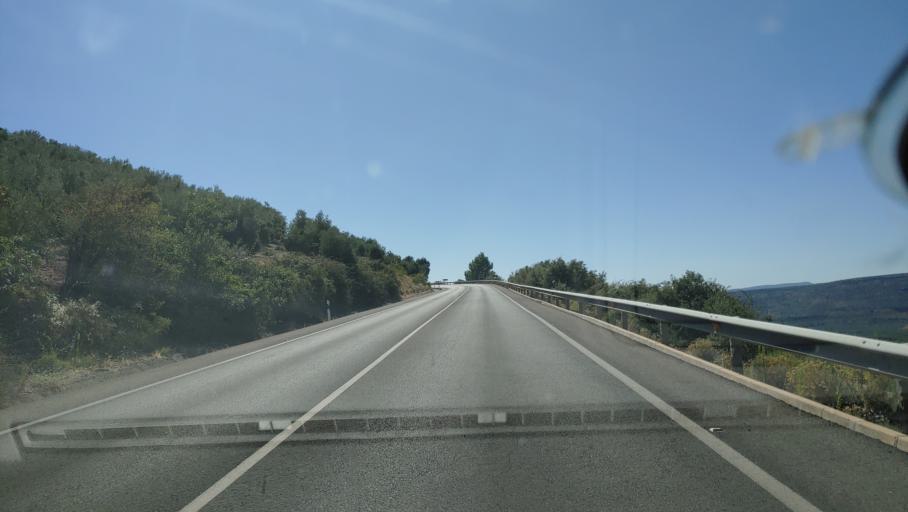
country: ES
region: Andalusia
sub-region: Provincia de Jaen
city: Campina
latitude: 38.2362
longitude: -2.9685
